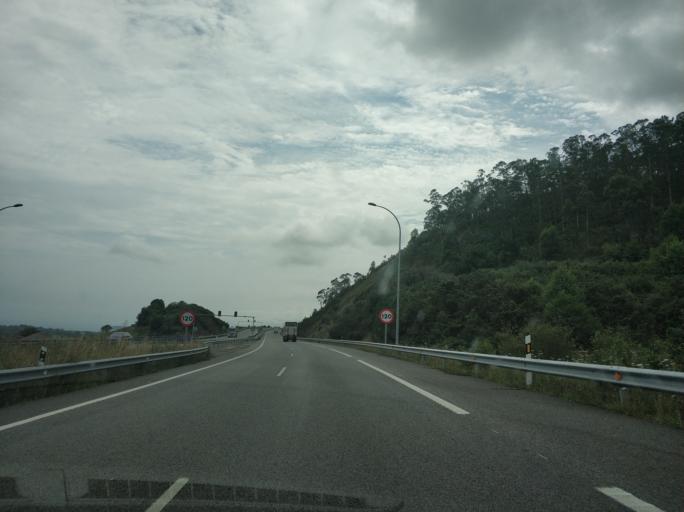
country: ES
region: Asturias
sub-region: Province of Asturias
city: Navia
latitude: 43.5350
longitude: -6.5984
